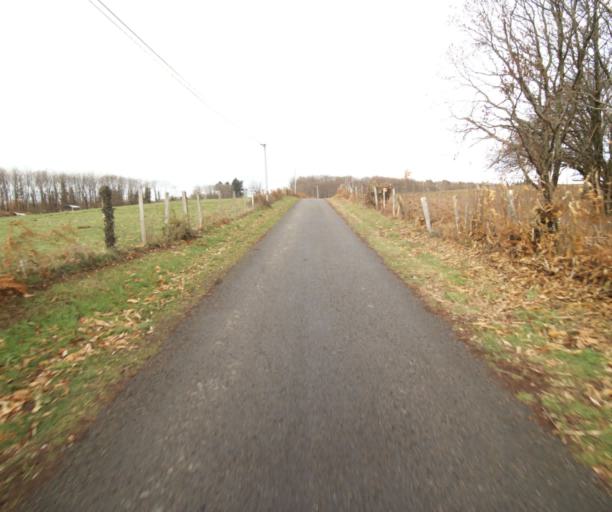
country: FR
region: Limousin
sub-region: Departement de la Correze
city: Saint-Mexant
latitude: 45.2787
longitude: 1.6492
